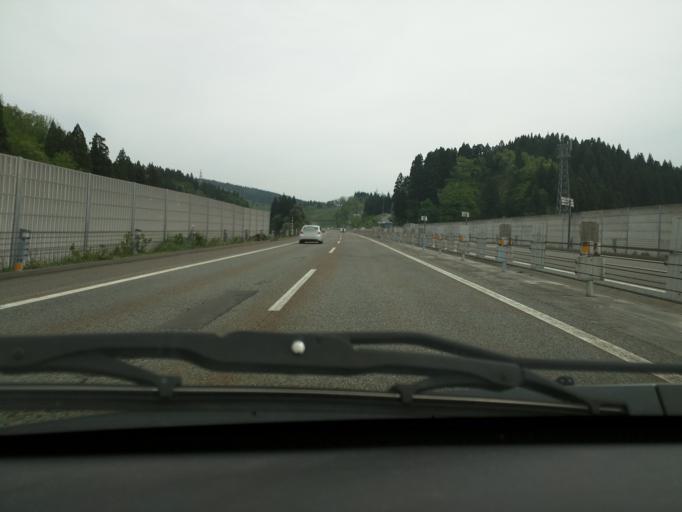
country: JP
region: Niigata
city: Ojiya
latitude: 37.2849
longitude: 138.7859
